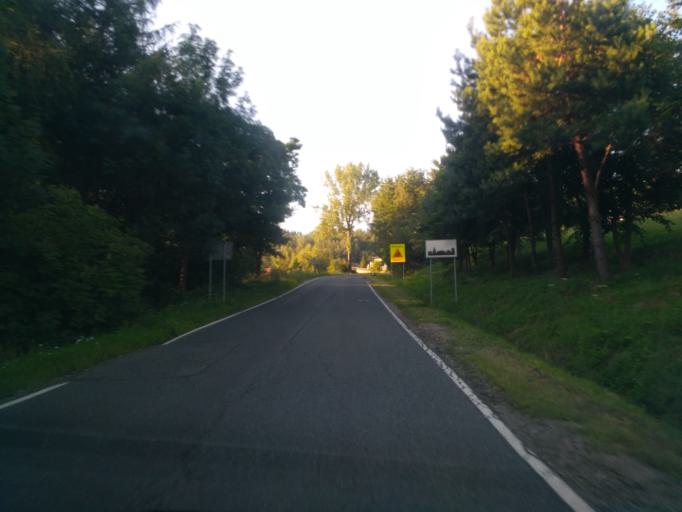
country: PL
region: Subcarpathian Voivodeship
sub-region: Powiat krosnienski
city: Korczyna
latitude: 49.7478
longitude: 21.8031
